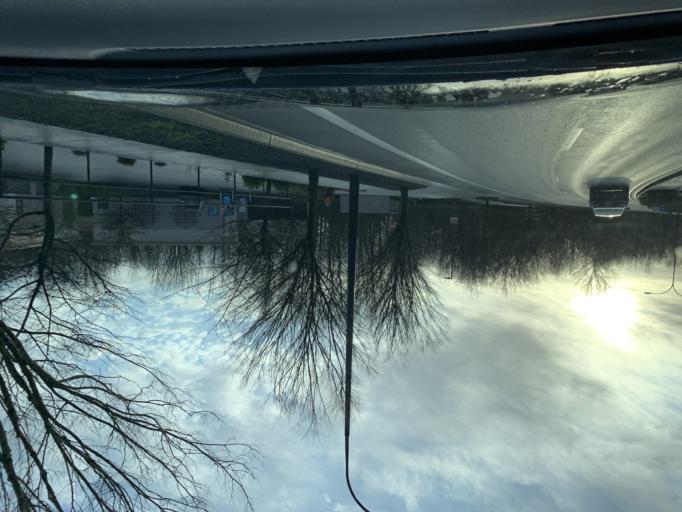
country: US
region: Washington
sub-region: Clark County
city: Mill Plain
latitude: 45.5938
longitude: -122.4779
